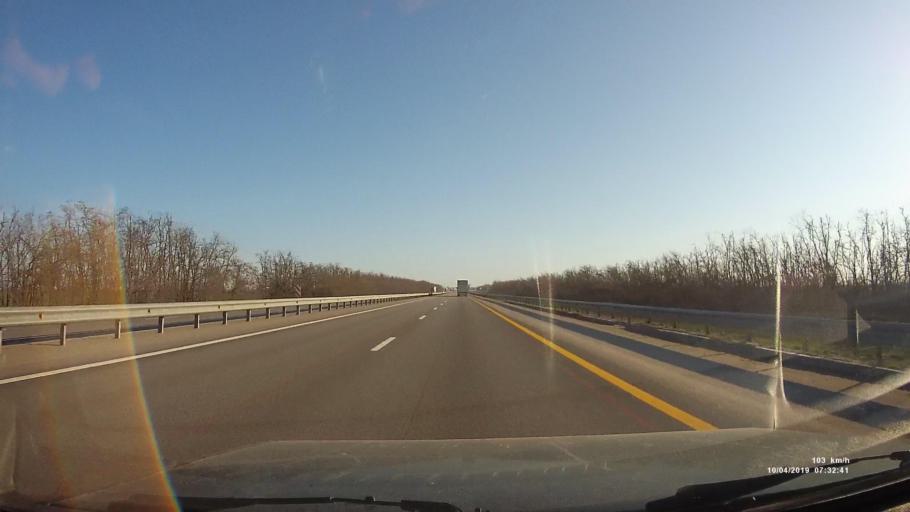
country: RU
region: Rostov
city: Zverevo
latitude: 48.0024
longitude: 40.2334
